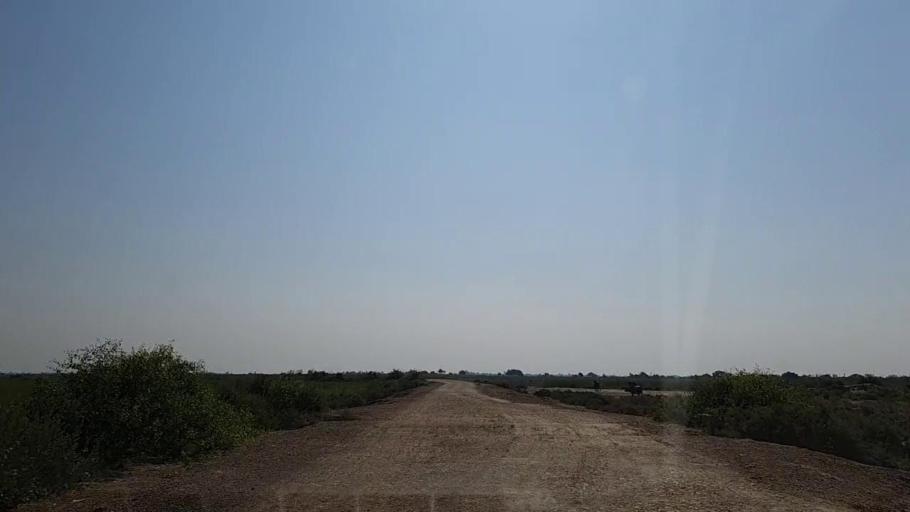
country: PK
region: Sindh
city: Chuhar Jamali
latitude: 24.4701
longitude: 68.0928
